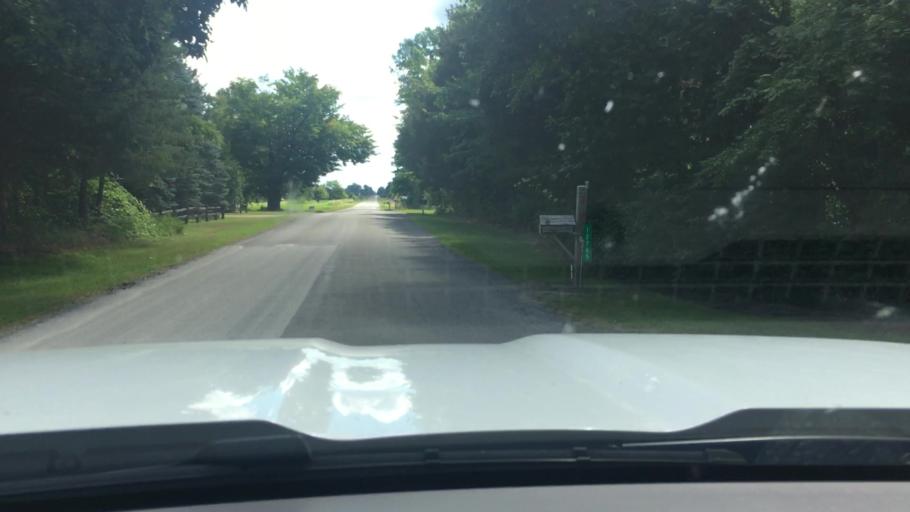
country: US
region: Michigan
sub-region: Saginaw County
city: Chesaning
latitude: 43.2156
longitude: -84.1647
